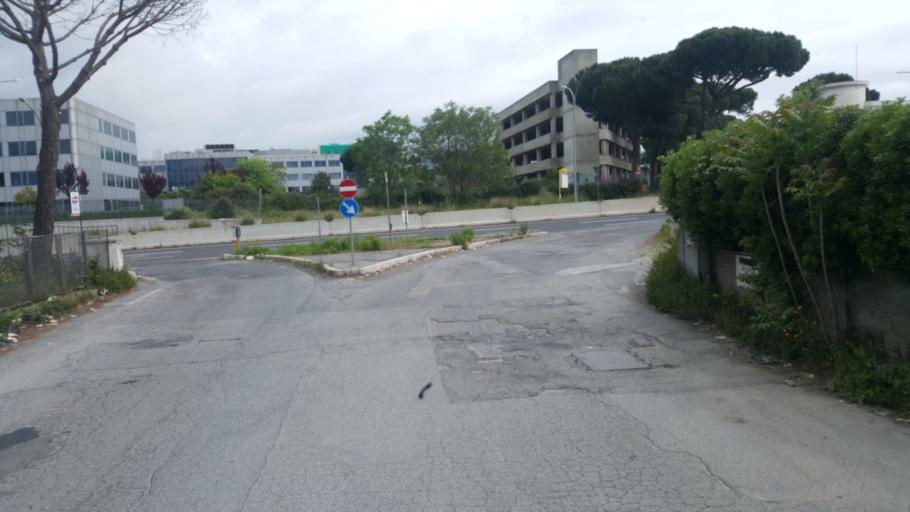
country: IT
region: Latium
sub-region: Citta metropolitana di Roma Capitale
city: Setteville
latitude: 41.9357
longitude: 12.6143
